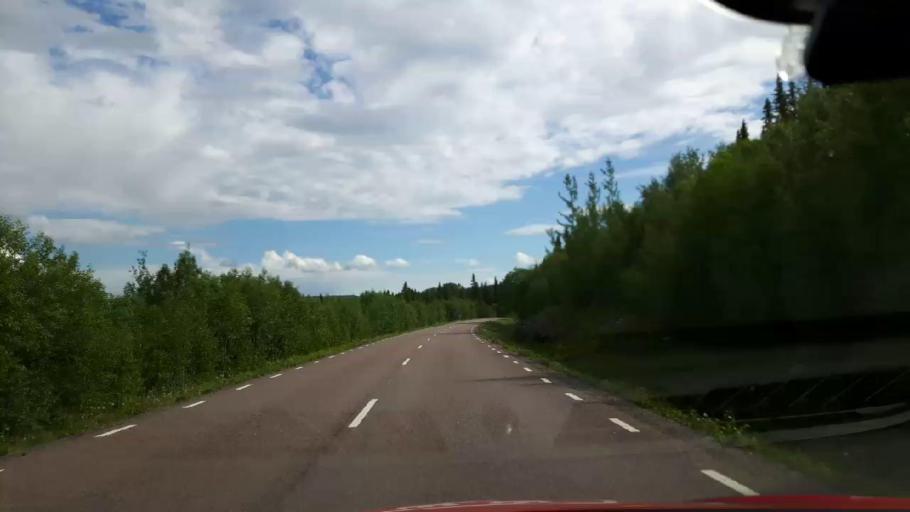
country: SE
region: Jaemtland
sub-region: Krokoms Kommun
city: Valla
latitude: 63.9238
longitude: 14.2143
